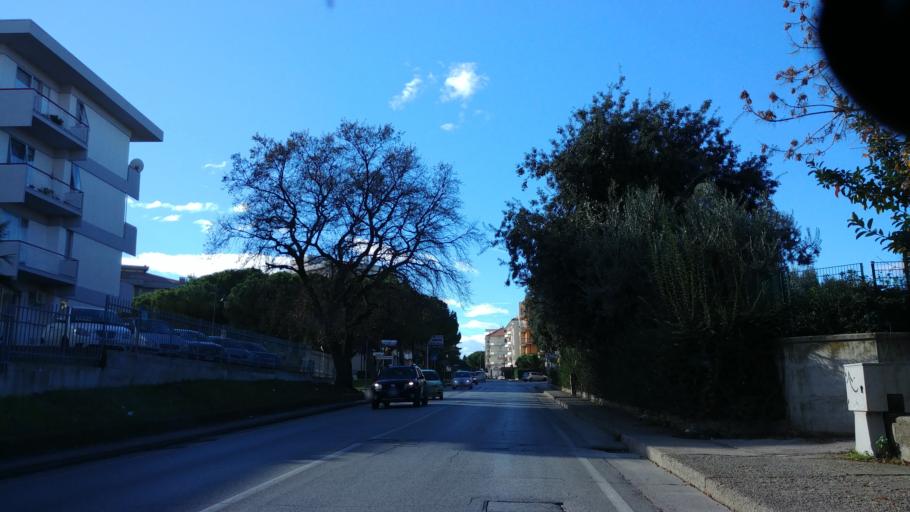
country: IT
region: Molise
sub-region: Provincia di Campobasso
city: Termoli
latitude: 41.9985
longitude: 14.9889
